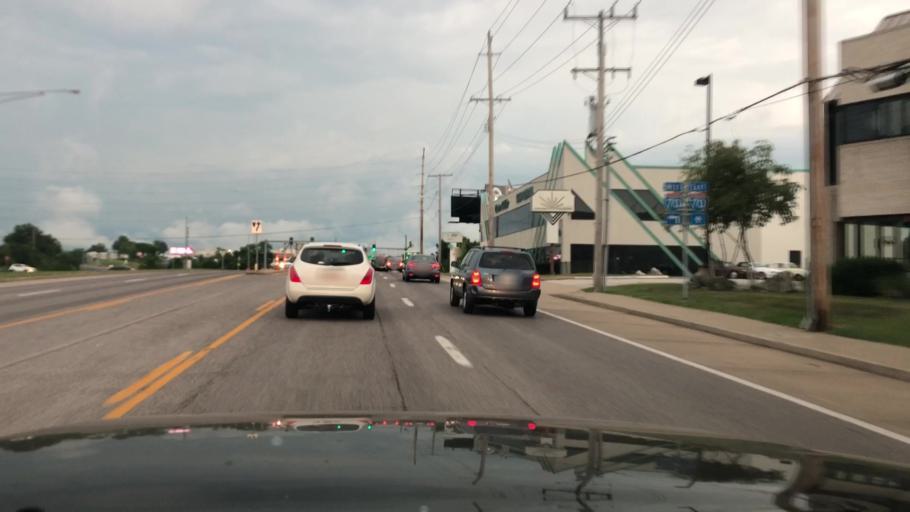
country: US
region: Missouri
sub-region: Saint Louis County
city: Bridgeton
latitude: 38.7450
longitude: -90.4157
